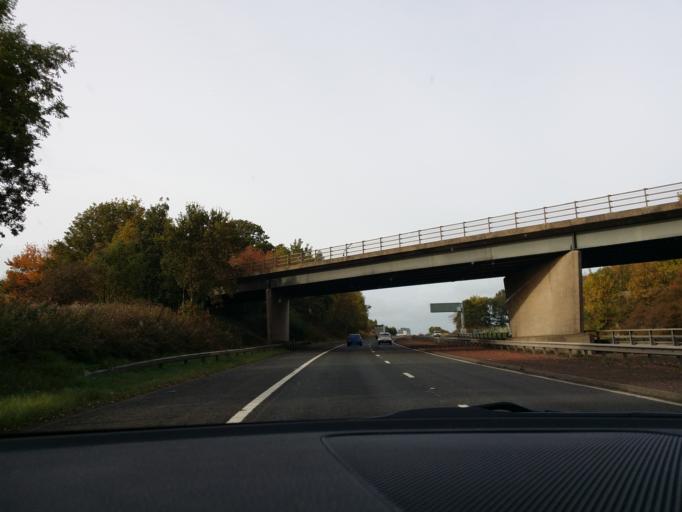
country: GB
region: Scotland
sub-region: Edinburgh
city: Kirkliston
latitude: 55.9610
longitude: -3.4419
